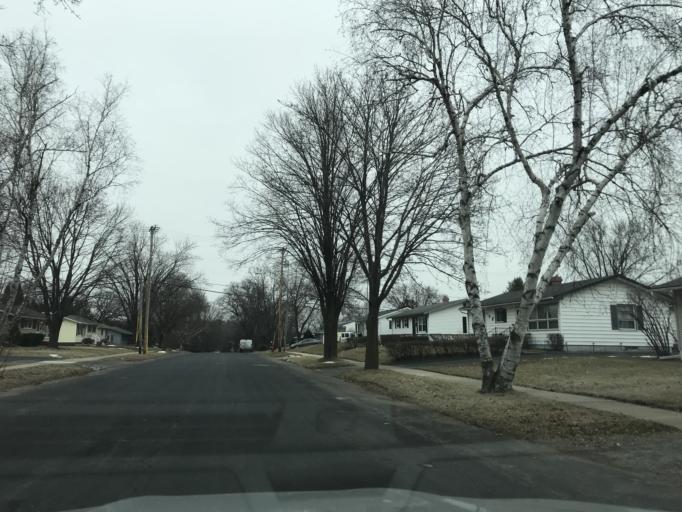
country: US
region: Wisconsin
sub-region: Dane County
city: Monona
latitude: 43.0946
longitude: -89.3059
